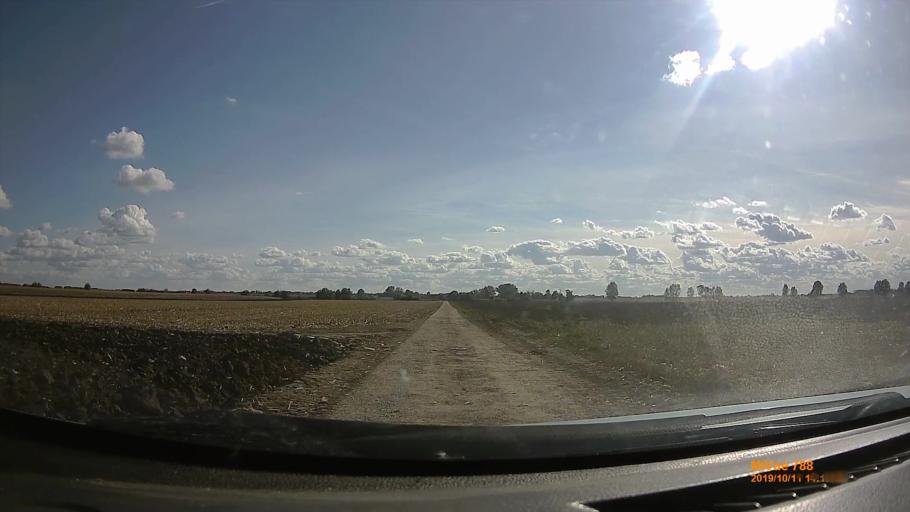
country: HU
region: Hajdu-Bihar
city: Hajduszoboszlo
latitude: 47.5349
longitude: 21.4014
